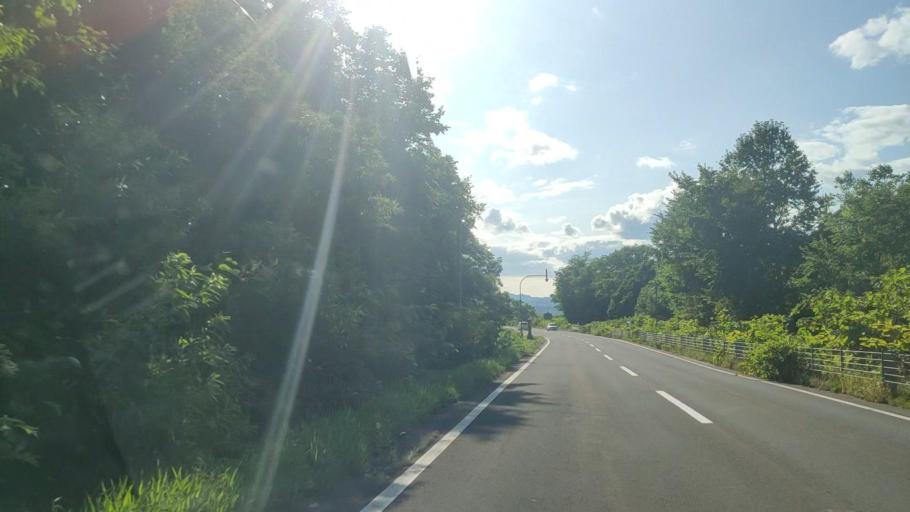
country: JP
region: Hokkaido
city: Nayoro
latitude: 44.7309
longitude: 142.0946
